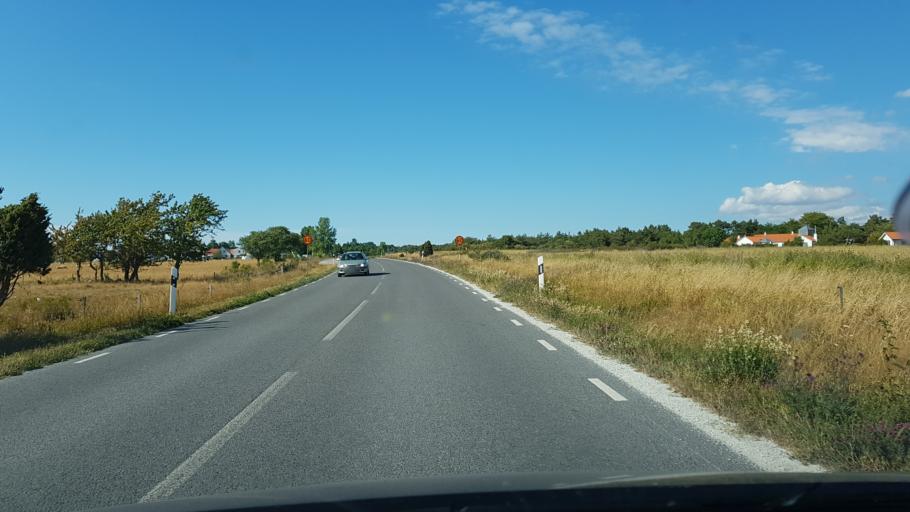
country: SE
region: Gotland
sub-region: Gotland
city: Klintehamn
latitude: 57.4270
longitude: 18.1497
